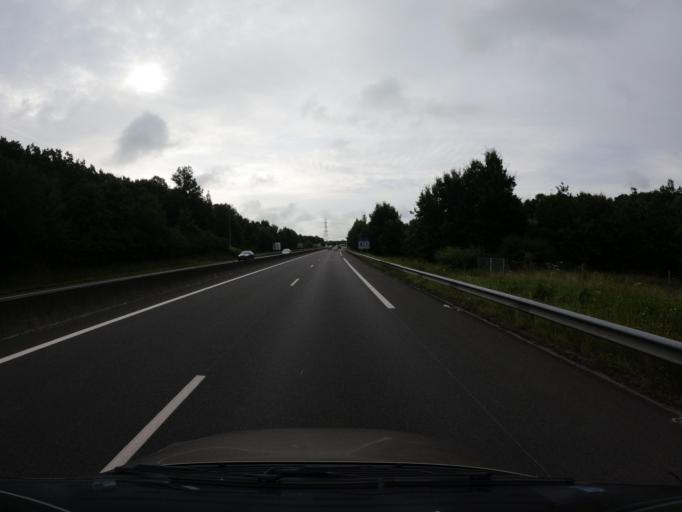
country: FR
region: Centre
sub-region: Departement d'Indre-et-Loire
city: Villandry
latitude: 47.3182
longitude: 0.5005
